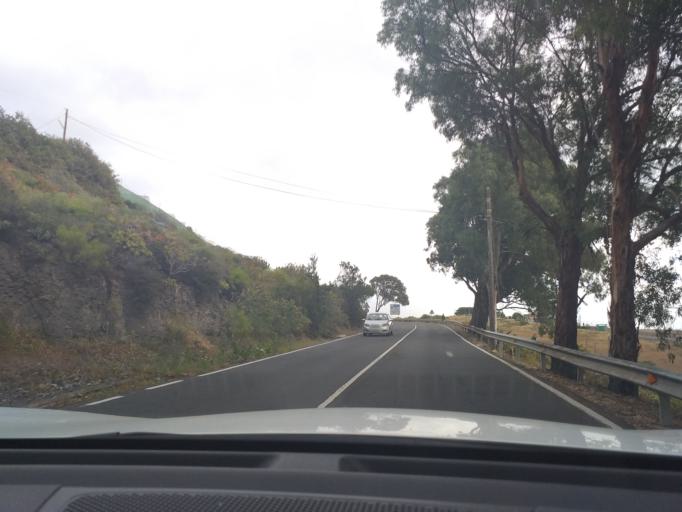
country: ES
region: Canary Islands
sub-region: Provincia de Las Palmas
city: Arucas
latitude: 28.1026
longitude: -15.4871
